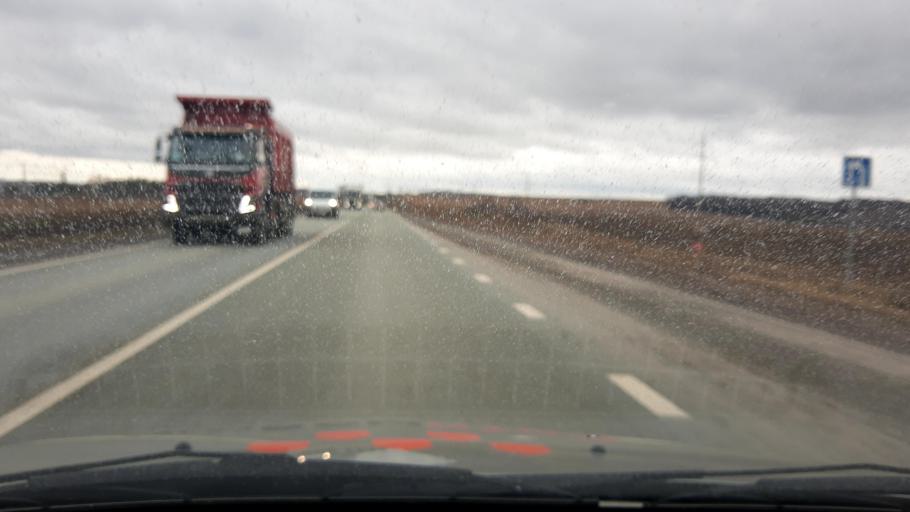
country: RU
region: Bashkortostan
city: Kabakovo
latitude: 54.6975
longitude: 56.2114
